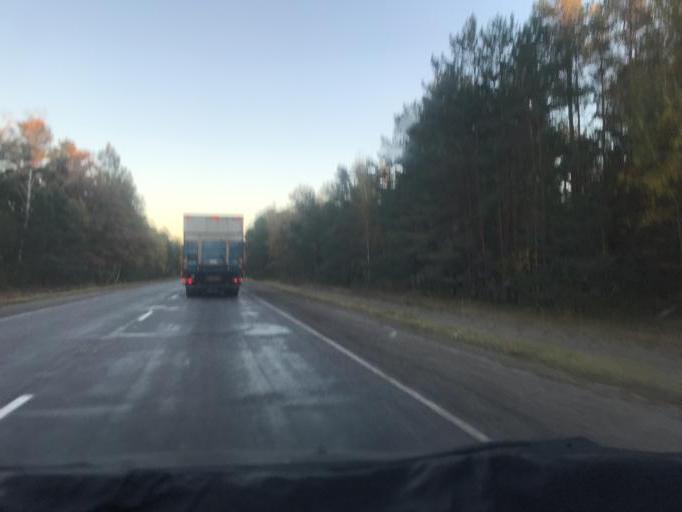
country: BY
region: Gomel
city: Mazyr
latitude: 52.2082
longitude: 29.0561
